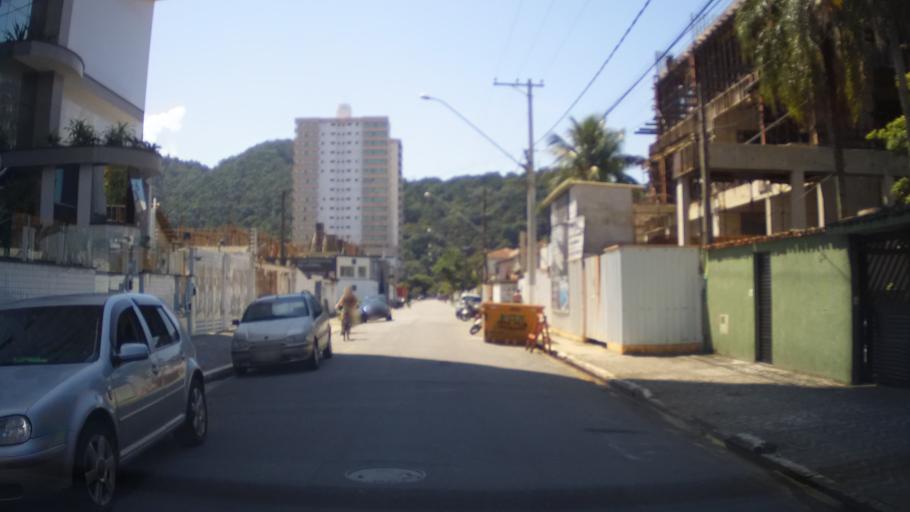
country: BR
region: Sao Paulo
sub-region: Praia Grande
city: Praia Grande
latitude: -24.0131
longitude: -46.3974
